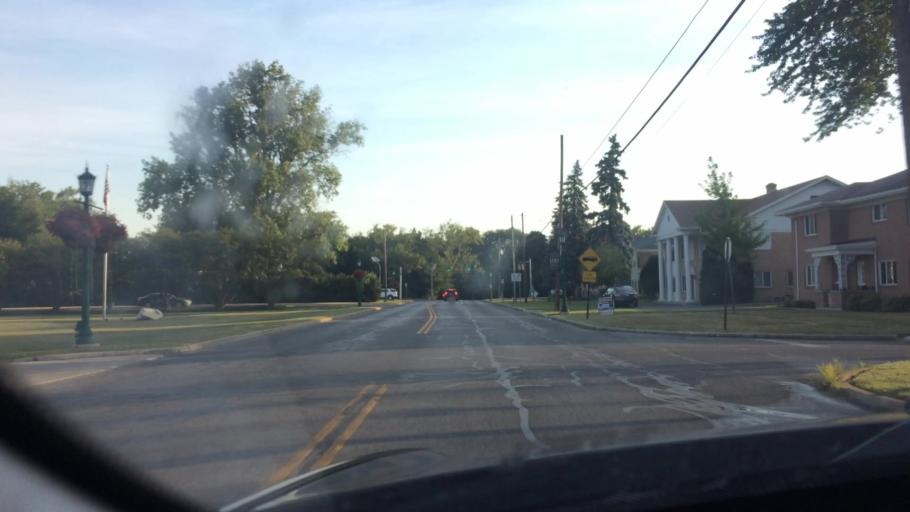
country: US
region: Ohio
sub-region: Lucas County
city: Ottawa Hills
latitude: 41.6612
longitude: -83.6411
